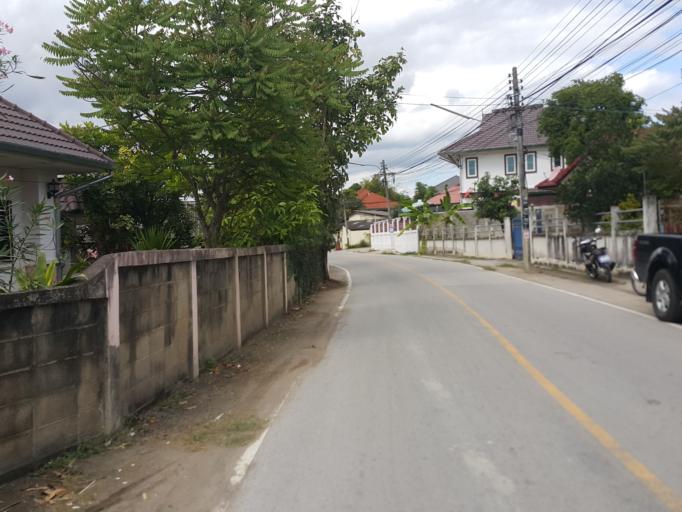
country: TH
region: Chiang Mai
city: San Sai
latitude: 18.8625
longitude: 99.1407
